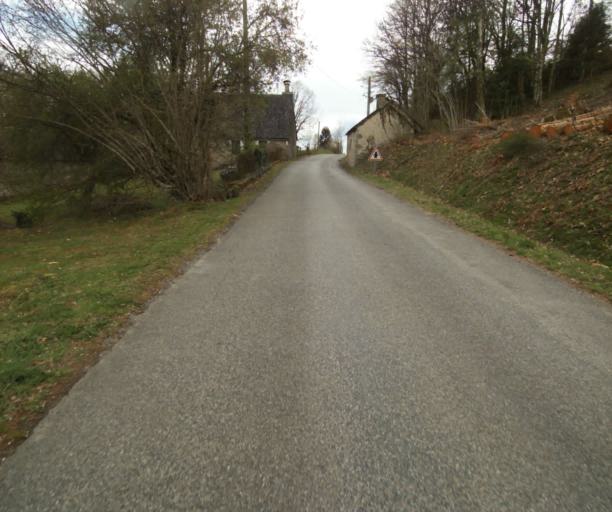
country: FR
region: Limousin
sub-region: Departement de la Correze
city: Argentat
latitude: 45.1910
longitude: 1.9573
